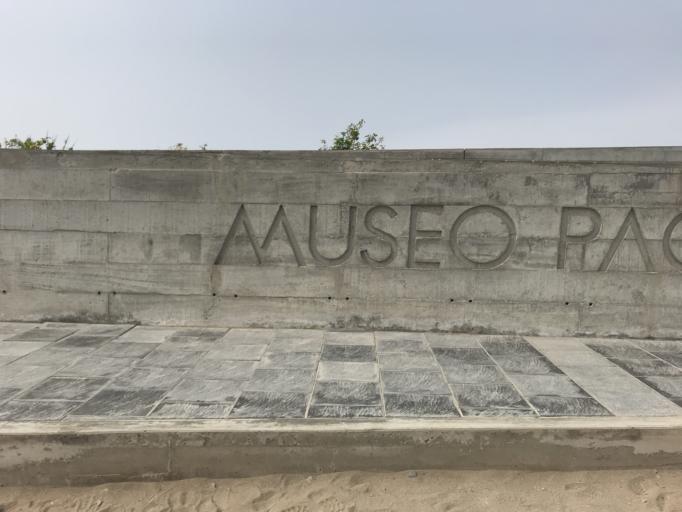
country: PE
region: Lima
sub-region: Lima
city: Punta Hermosa
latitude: -12.2554
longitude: -76.9074
